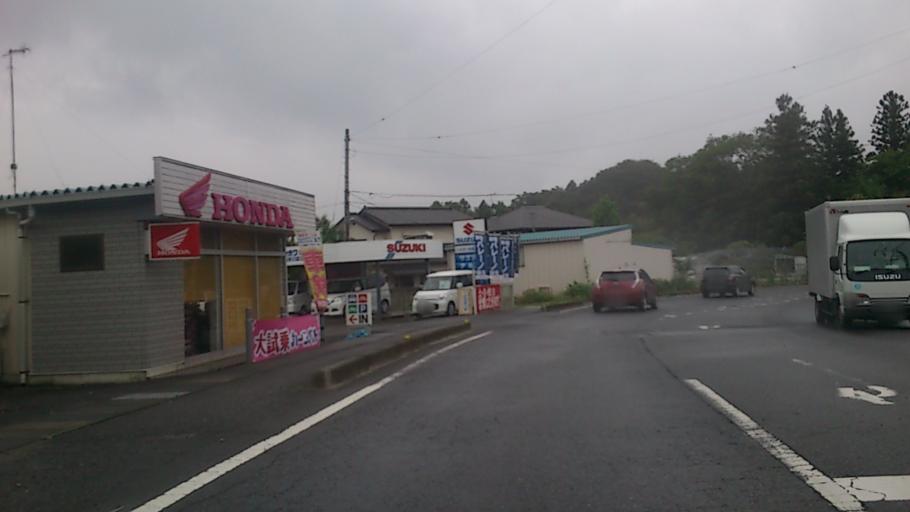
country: JP
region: Tochigi
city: Karasuyama
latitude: 36.7593
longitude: 140.1276
